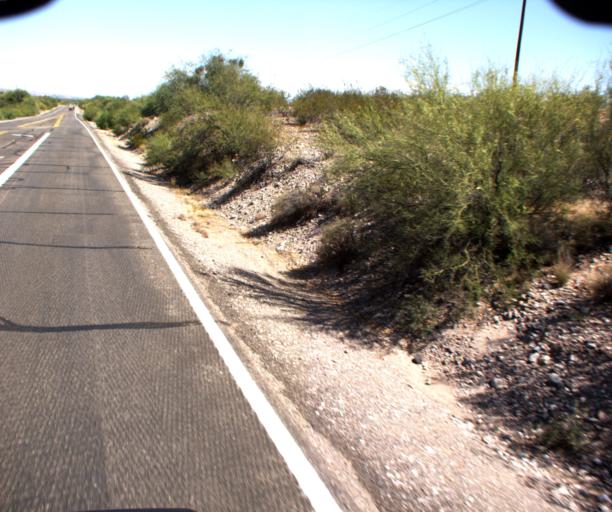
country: US
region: Arizona
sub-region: Pinal County
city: Mammoth
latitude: 32.7912
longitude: -110.6730
